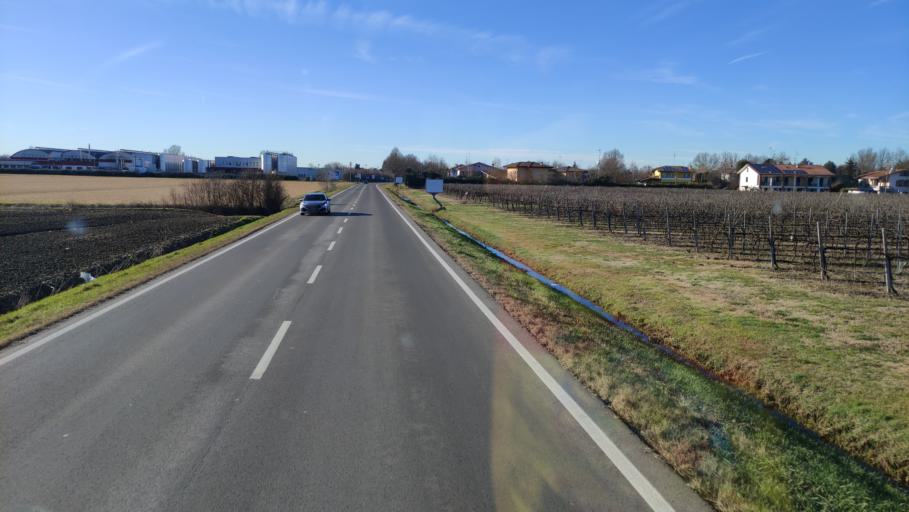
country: IT
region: Emilia-Romagna
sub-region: Provincia di Reggio Emilia
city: Campagnola Emilia
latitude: 44.8357
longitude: 10.7661
